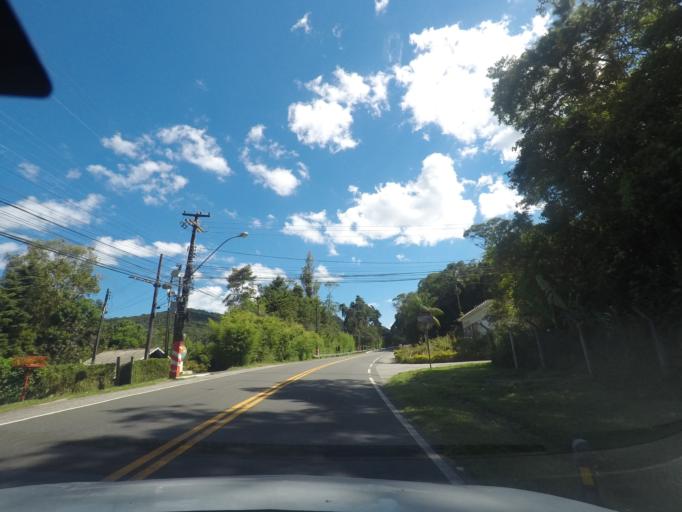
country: BR
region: Rio de Janeiro
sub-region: Teresopolis
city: Teresopolis
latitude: -22.4513
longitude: -42.9822
